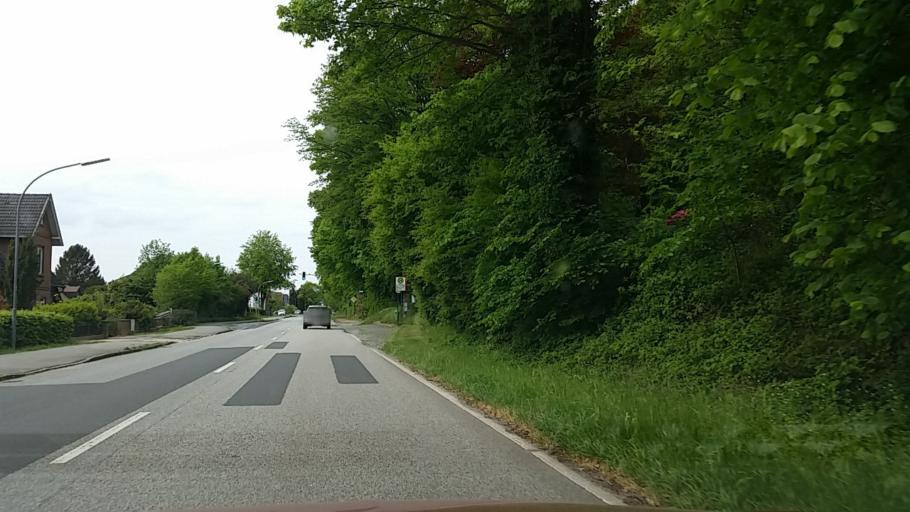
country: DE
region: Schleswig-Holstein
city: Bornsen
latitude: 53.4671
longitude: 10.2884
